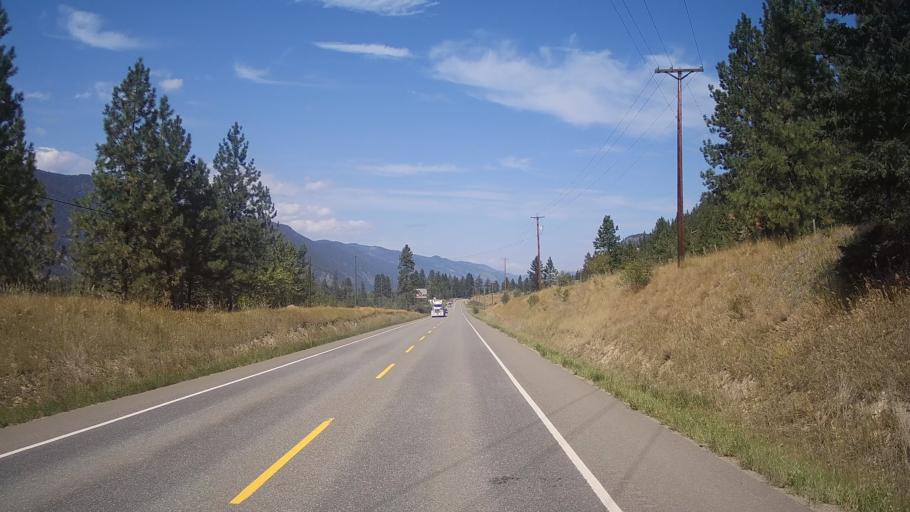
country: CA
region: British Columbia
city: Kamloops
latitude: 50.9543
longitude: -120.2348
